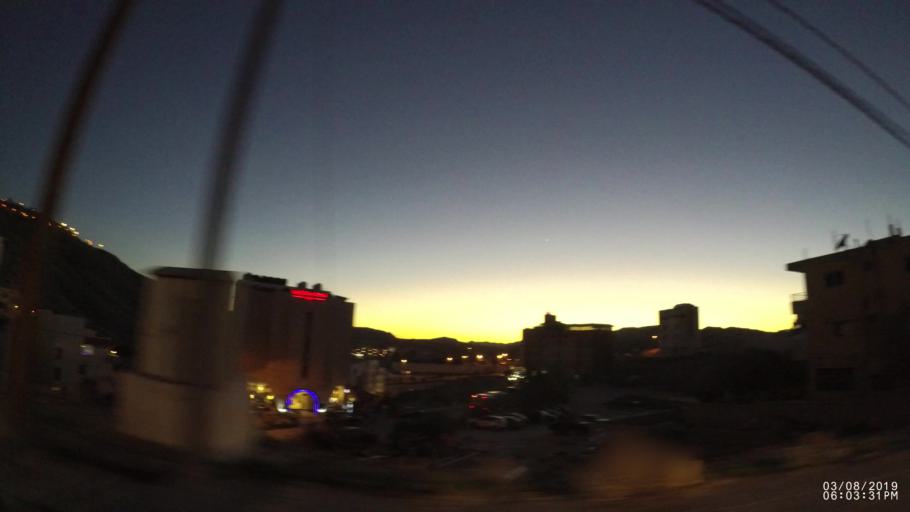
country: JO
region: Ma'an
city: Petra
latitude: 30.3266
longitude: 35.4707
